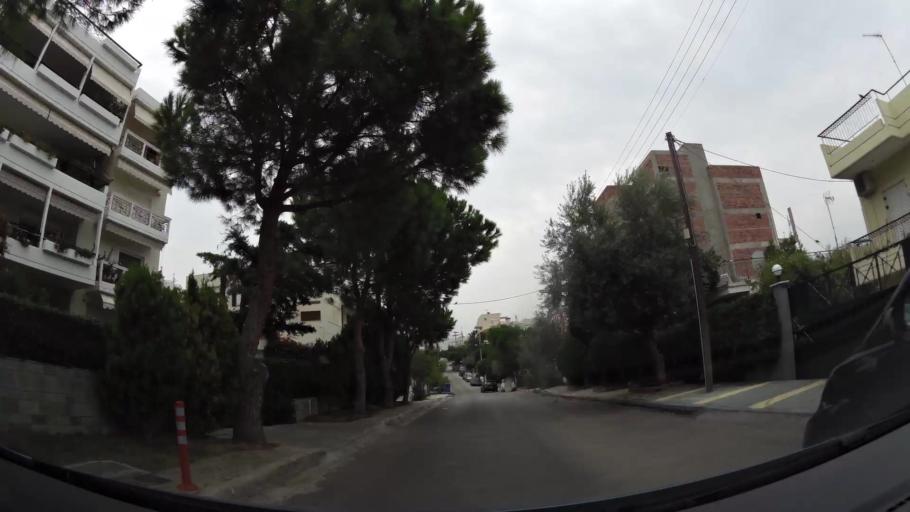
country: GR
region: Attica
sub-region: Nomarchia Athinas
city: Alimos
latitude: 37.9106
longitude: 23.7248
